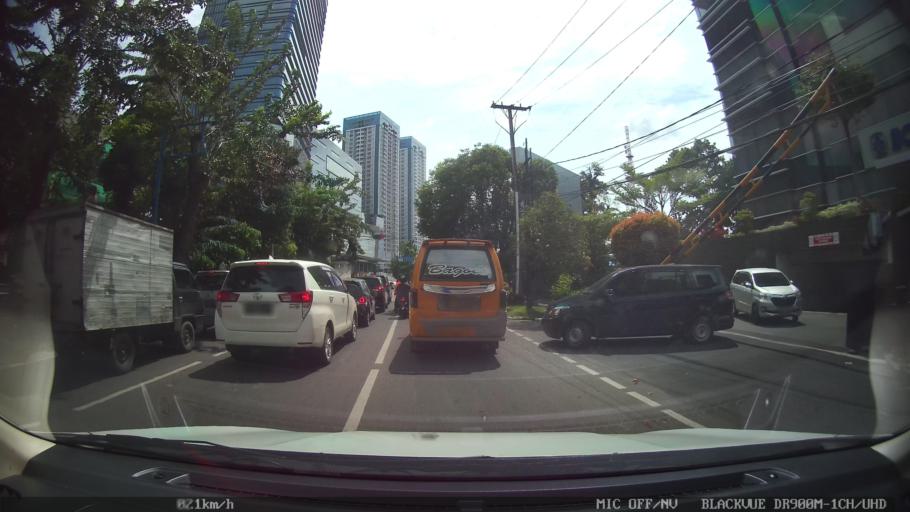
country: ID
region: North Sumatra
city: Medan
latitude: 3.5961
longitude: 98.6762
